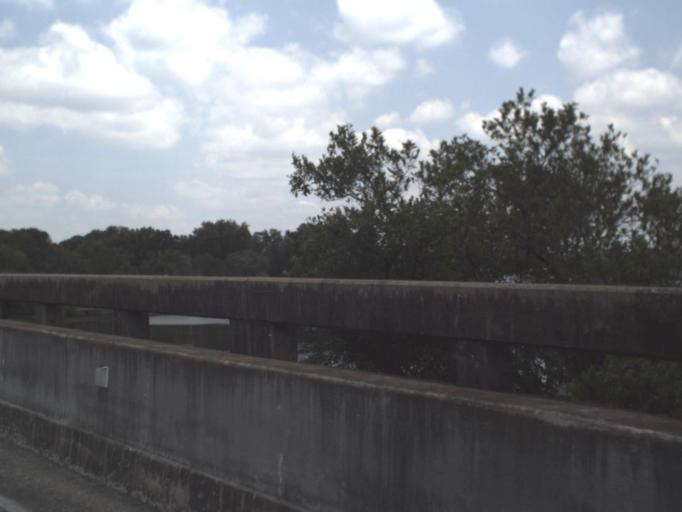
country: US
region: Florida
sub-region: Duval County
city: Jacksonville
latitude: 30.3898
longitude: -81.6620
